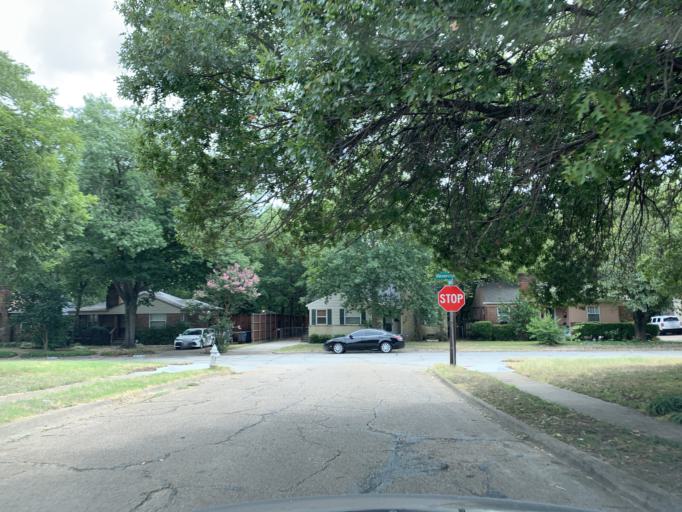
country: US
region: Texas
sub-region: Dallas County
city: Cockrell Hill
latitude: 32.7509
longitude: -96.8639
